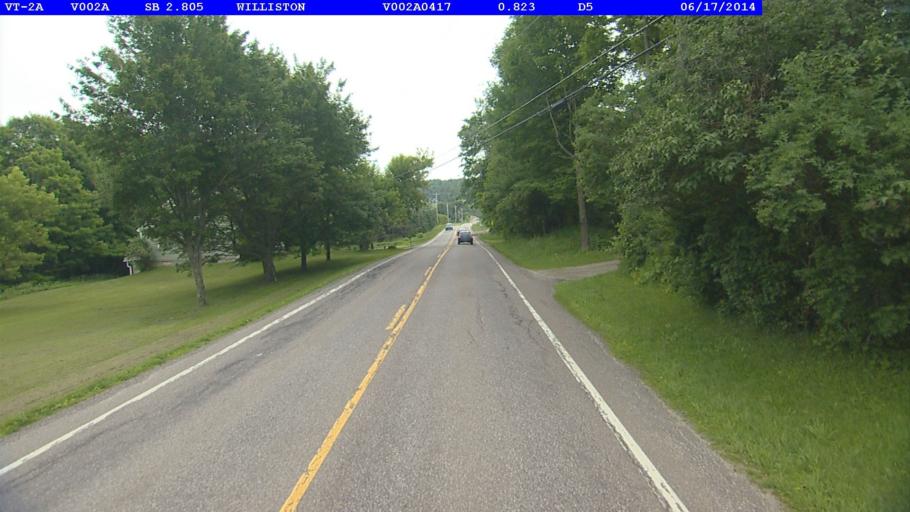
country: US
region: Vermont
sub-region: Chittenden County
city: Williston
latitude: 44.4096
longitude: -73.1250
